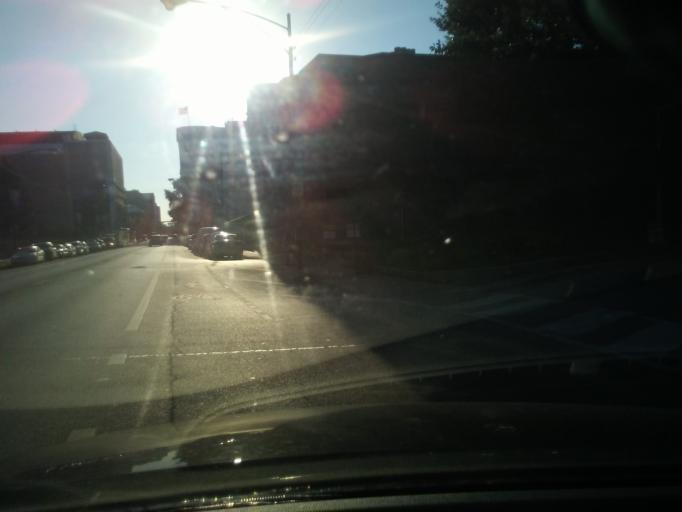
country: US
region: Illinois
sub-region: Cook County
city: Lincolnwood
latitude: 41.9689
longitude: -87.6631
